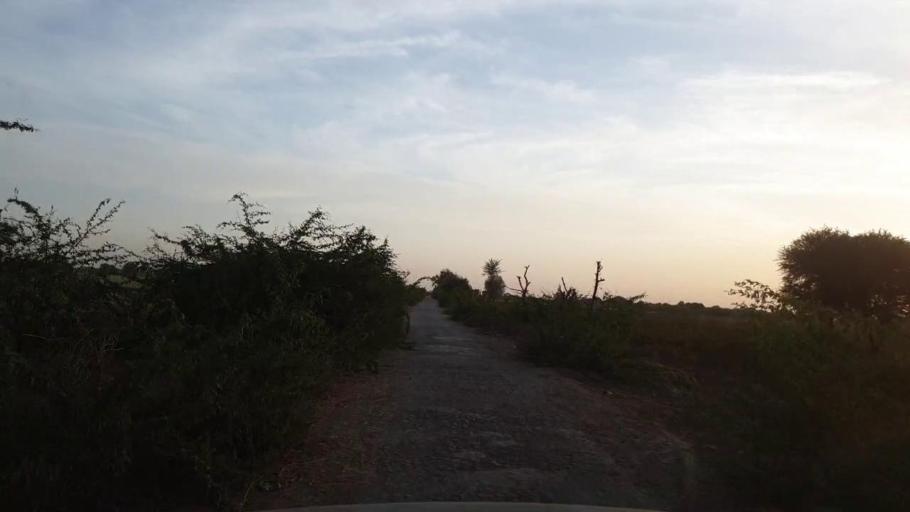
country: PK
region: Sindh
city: Kunri
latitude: 25.1128
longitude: 69.5632
